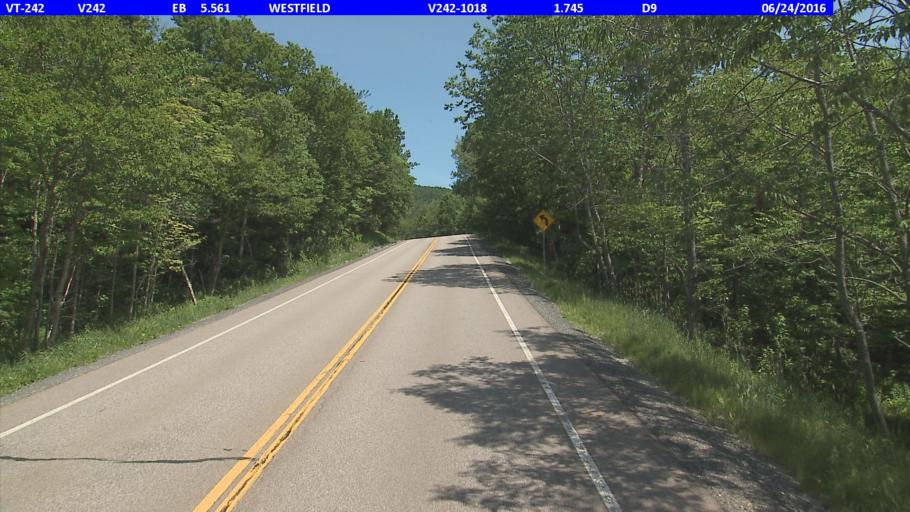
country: US
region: Vermont
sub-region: Franklin County
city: Richford
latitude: 44.9046
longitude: -72.5145
